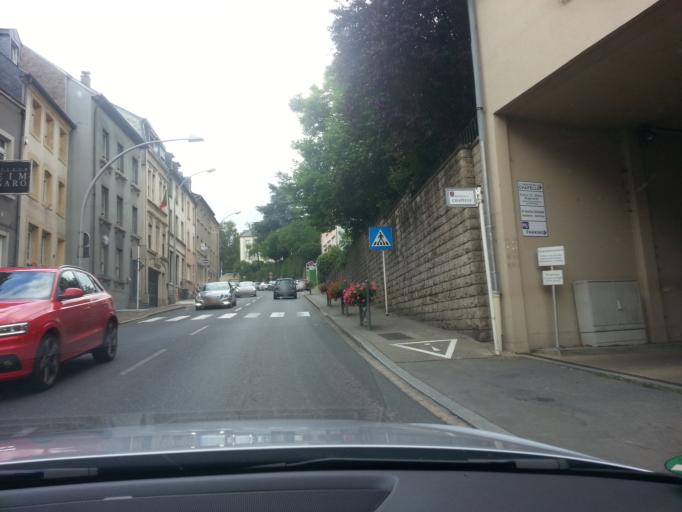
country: LU
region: Grevenmacher
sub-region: Canton de Remich
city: Remich
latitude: 49.5450
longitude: 6.3676
